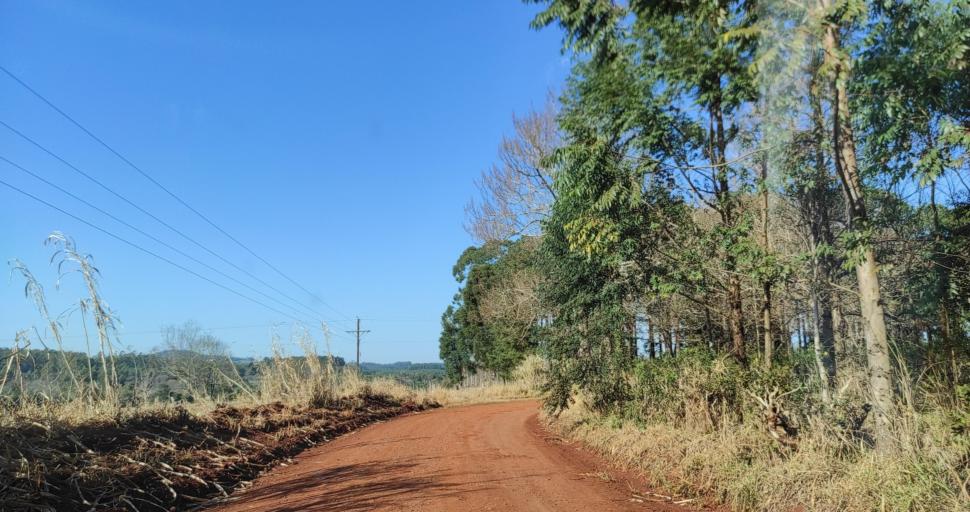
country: AR
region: Misiones
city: Puerto Rico
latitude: -26.8639
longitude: -55.0269
